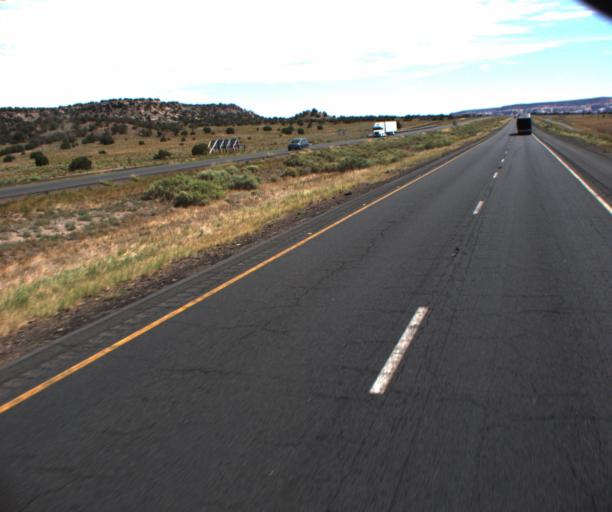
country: US
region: Arizona
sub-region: Apache County
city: Houck
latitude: 35.2926
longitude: -109.1478
